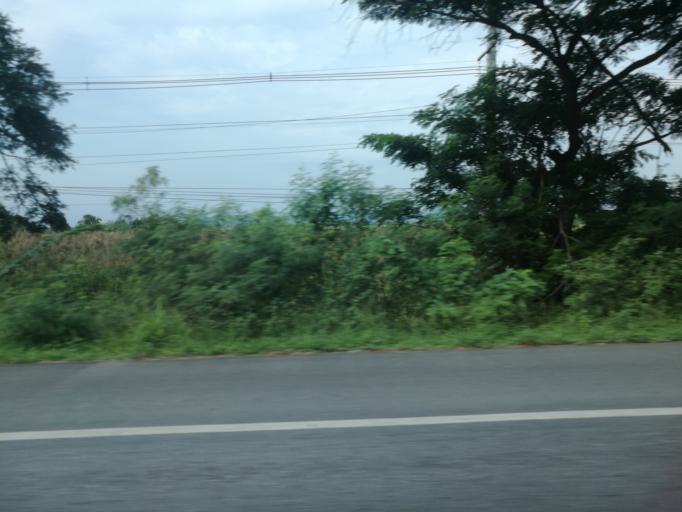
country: TH
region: Prachuap Khiri Khan
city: Hua Hin
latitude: 12.5361
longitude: 99.8770
